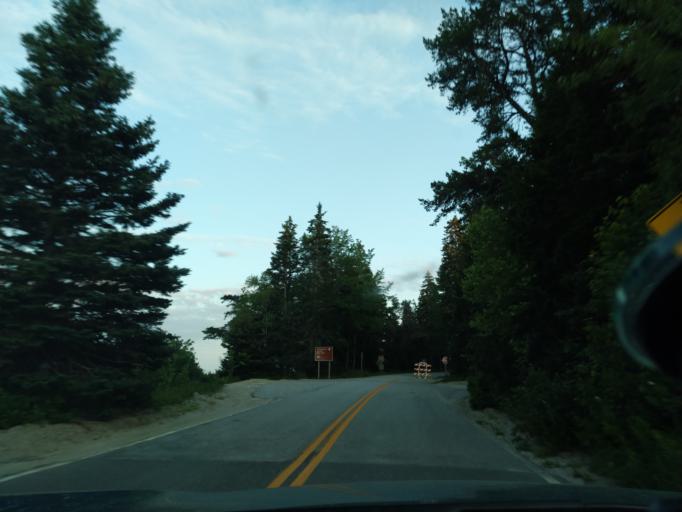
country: US
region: Maine
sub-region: Hancock County
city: Gouldsboro
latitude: 44.3649
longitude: -68.0384
